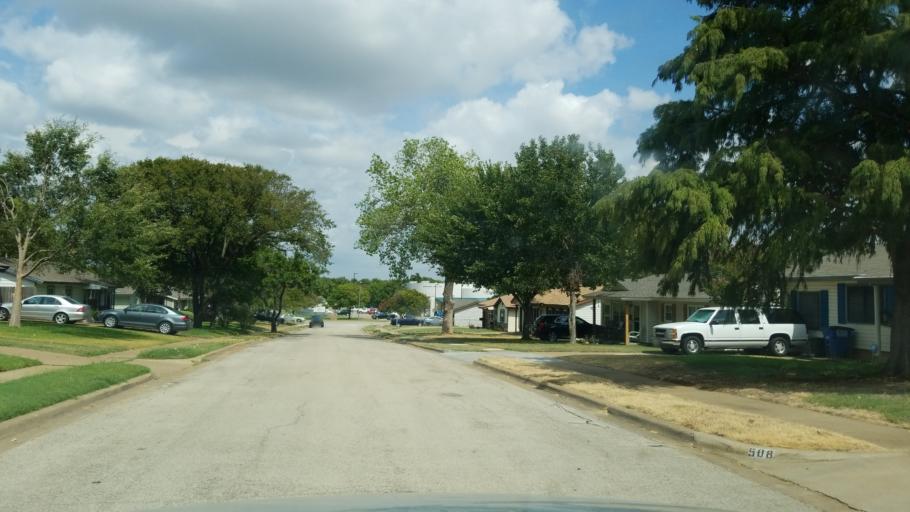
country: US
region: Texas
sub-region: Tarrant County
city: Euless
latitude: 32.8433
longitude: -97.0870
